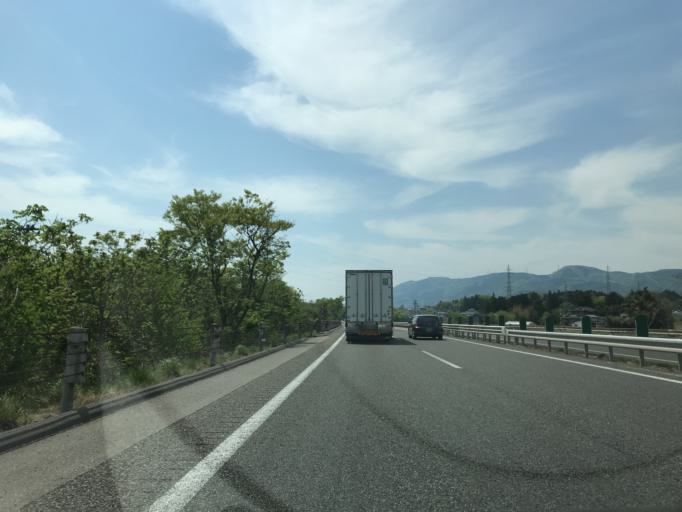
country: JP
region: Miyagi
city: Shiroishi
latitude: 38.0286
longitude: 140.6253
